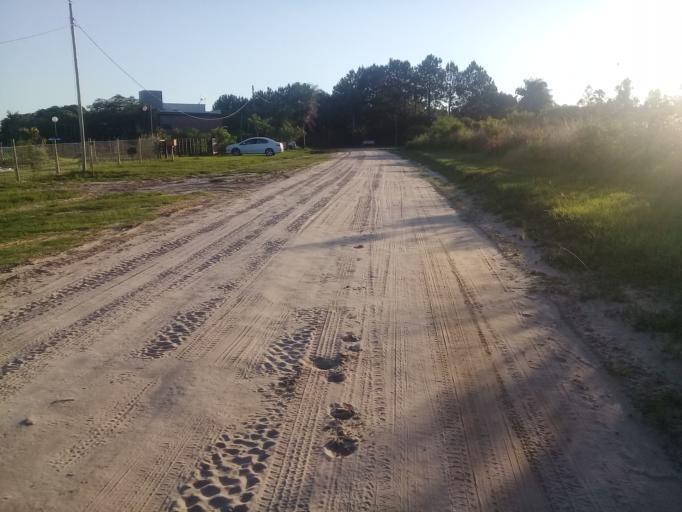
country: AR
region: Corrientes
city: San Luis del Palmar
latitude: -27.4673
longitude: -58.6629
